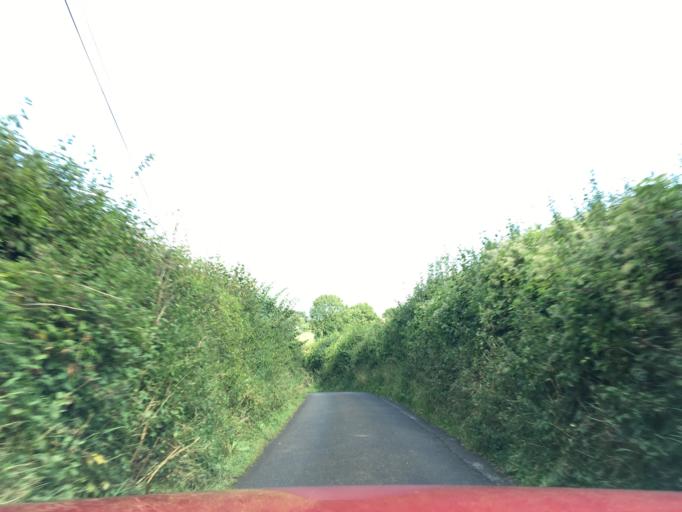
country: GB
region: England
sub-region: South Gloucestershire
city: Tytherington
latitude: 51.5996
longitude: -2.4745
